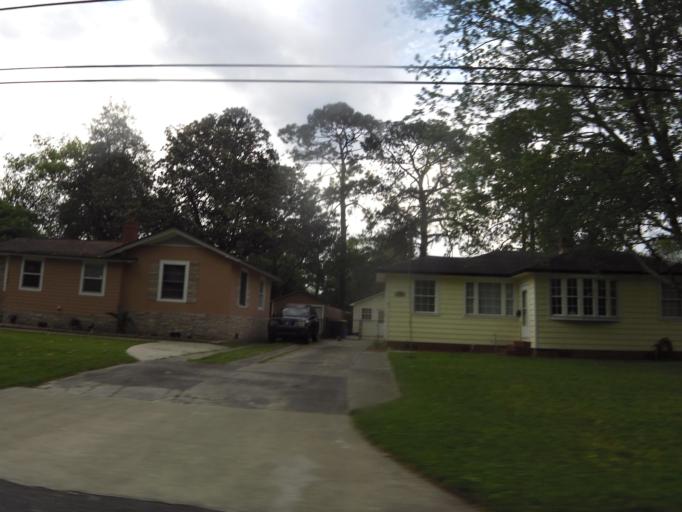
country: US
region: Florida
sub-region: Duval County
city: Jacksonville
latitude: 30.2868
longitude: -81.7261
